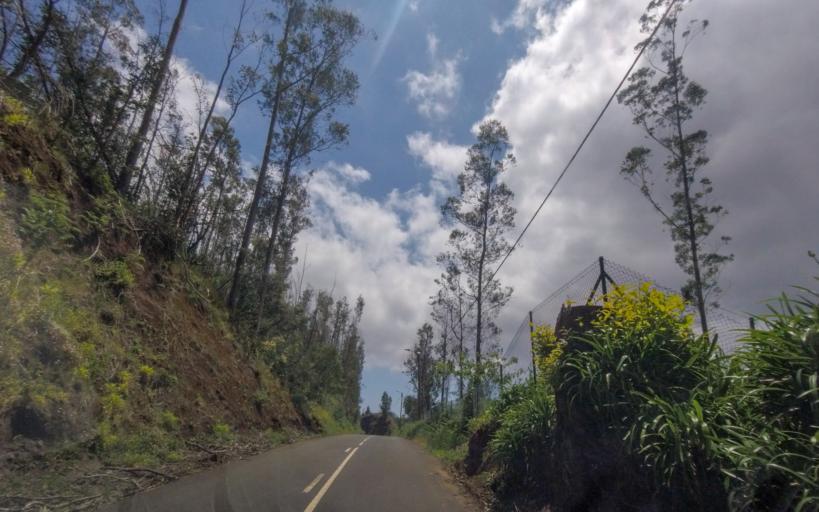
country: PT
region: Madeira
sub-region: Funchal
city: Nossa Senhora do Monte
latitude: 32.6816
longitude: -16.8837
